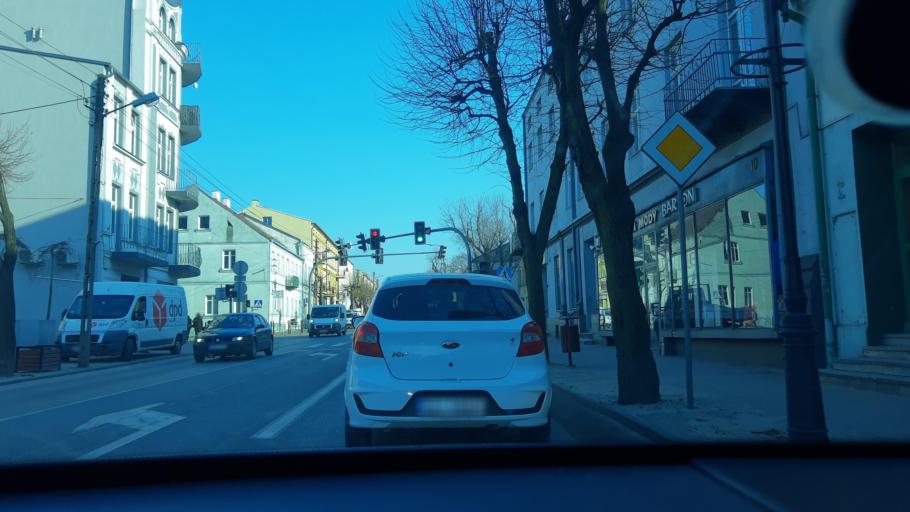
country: PL
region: Lodz Voivodeship
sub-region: Powiat zdunskowolski
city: Zdunska Wola
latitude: 51.6012
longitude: 18.9357
